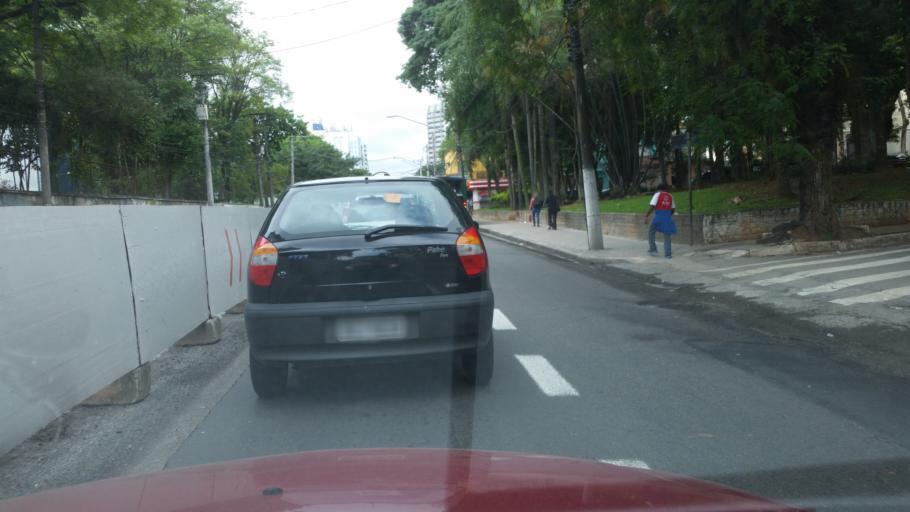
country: BR
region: Sao Paulo
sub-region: Diadema
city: Diadema
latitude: -23.6486
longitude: -46.7031
